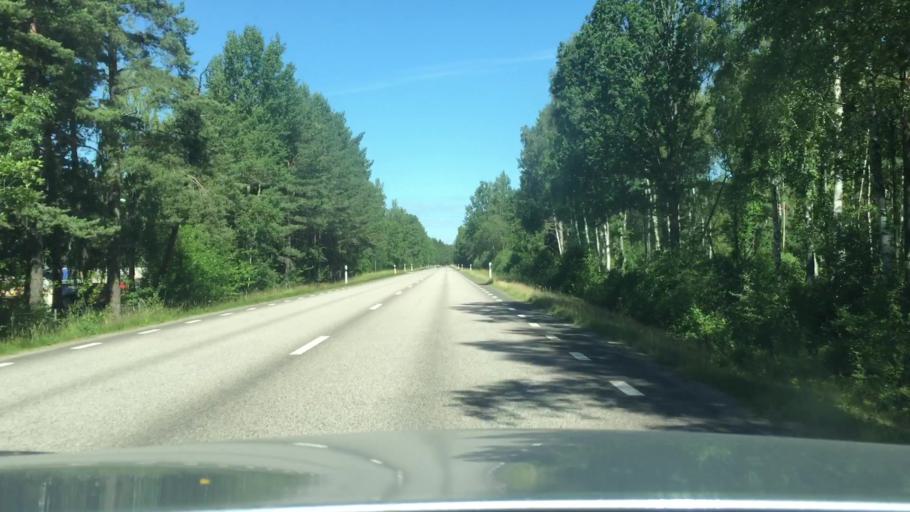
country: SE
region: Vaestra Goetaland
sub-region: Mariestads Kommun
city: Mariestad
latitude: 58.6720
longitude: 13.8552
